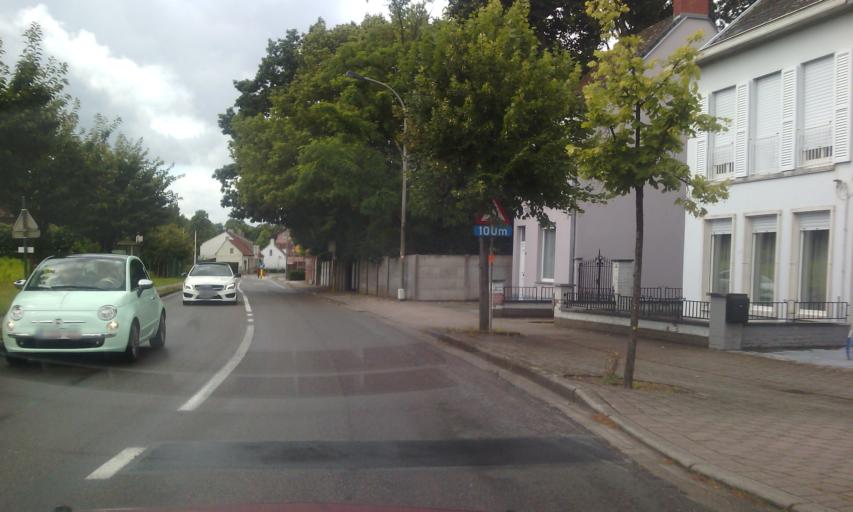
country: BE
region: Flanders
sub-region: Provincie Oost-Vlaanderen
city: Laarne
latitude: 51.0291
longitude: 3.8555
